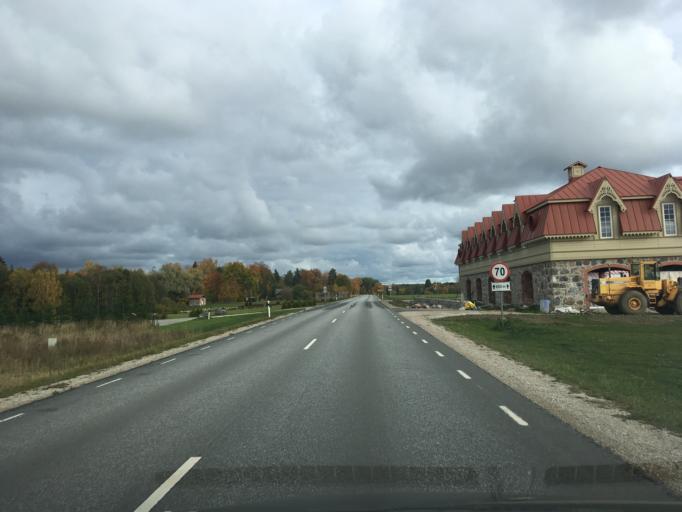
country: EE
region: Harju
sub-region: Anija vald
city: Kehra
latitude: 59.2786
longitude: 25.3685
